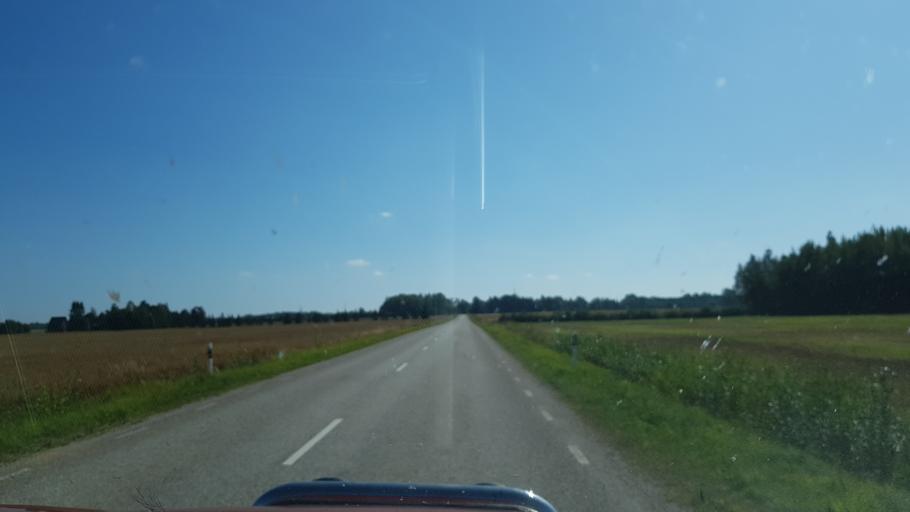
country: EE
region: Polvamaa
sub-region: Polva linn
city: Polva
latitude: 58.2161
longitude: 27.2433
